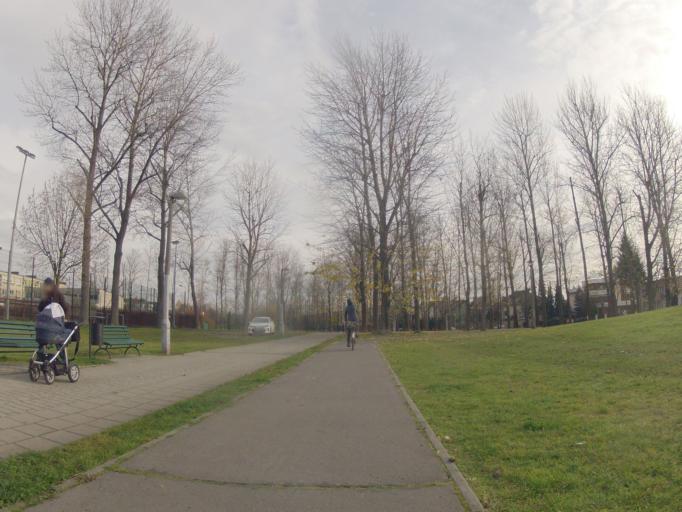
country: PL
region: Lesser Poland Voivodeship
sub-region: Powiat krakowski
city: Rzaska
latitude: 50.0769
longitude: 19.8827
